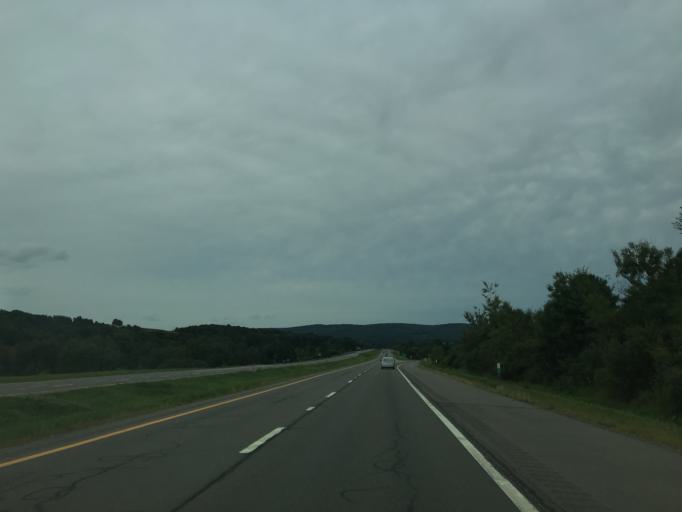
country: US
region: New York
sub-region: Chenango County
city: Greene
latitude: 42.1874
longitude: -75.6439
